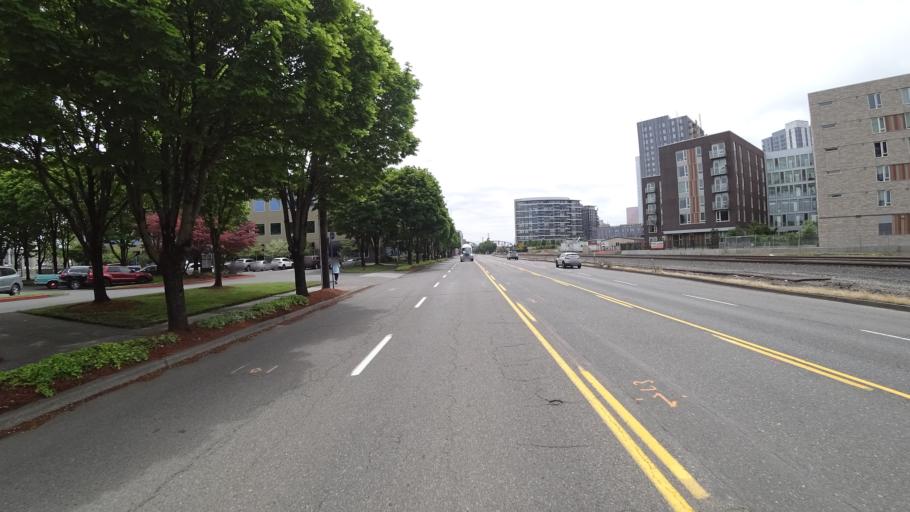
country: US
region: Oregon
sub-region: Multnomah County
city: Portland
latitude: 45.5354
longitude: -122.6842
